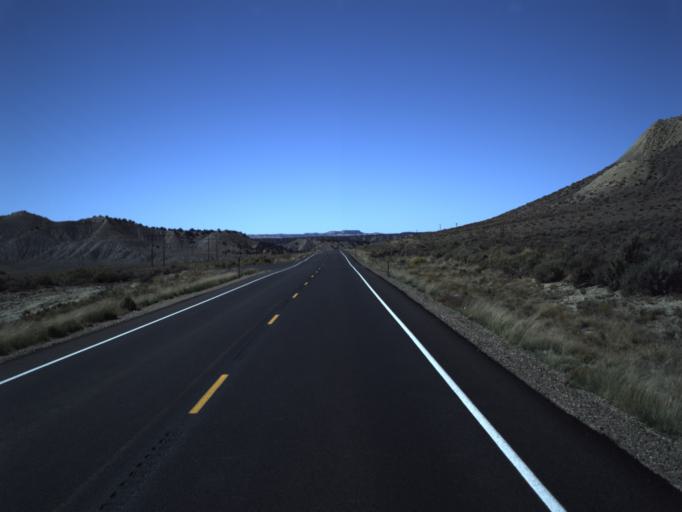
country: US
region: Utah
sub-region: Garfield County
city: Panguitch
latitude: 37.5928
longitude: -111.9339
